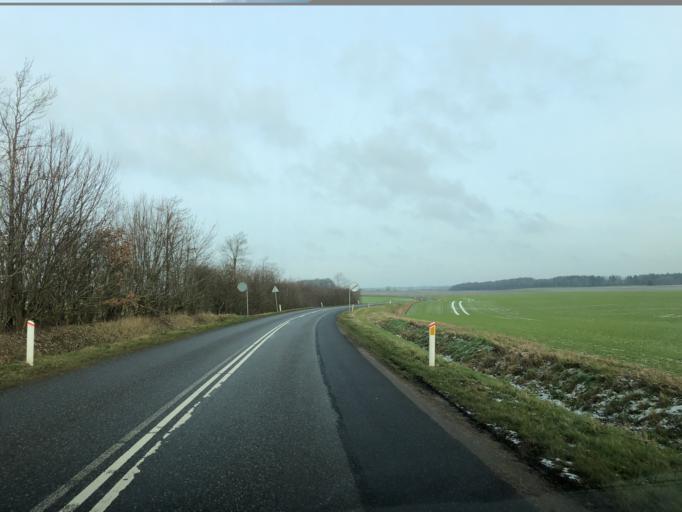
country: DK
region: South Denmark
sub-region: Vejle Kommune
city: Jelling
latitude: 55.7776
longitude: 9.4282
